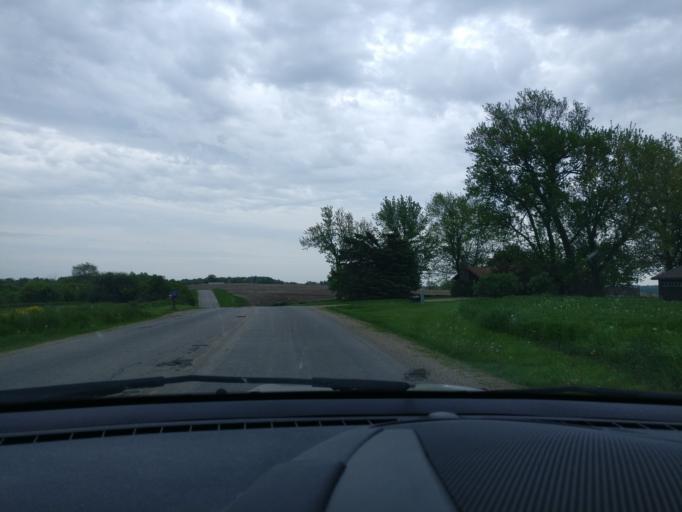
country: US
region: Wisconsin
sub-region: Lafayette County
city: Darlington
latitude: 42.7509
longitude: -90.0024
